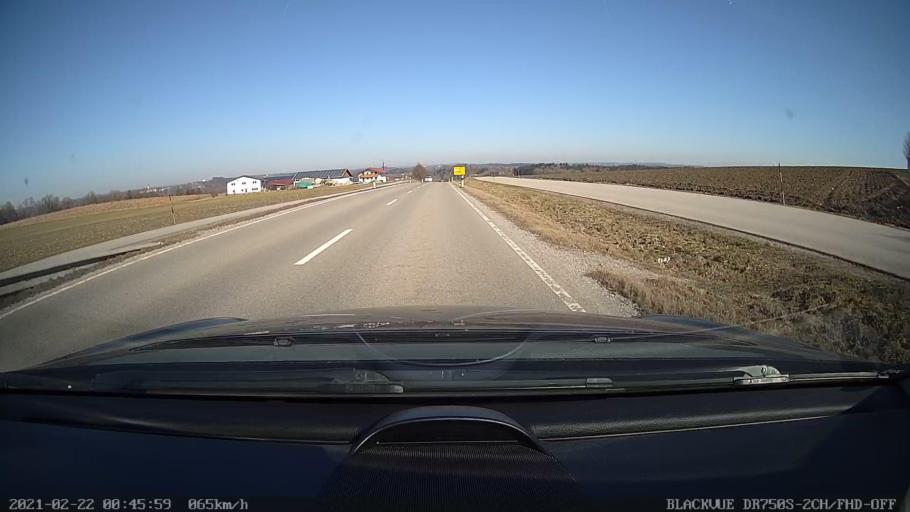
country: DE
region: Bavaria
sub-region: Upper Bavaria
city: Griesstatt
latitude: 47.9983
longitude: 12.1765
